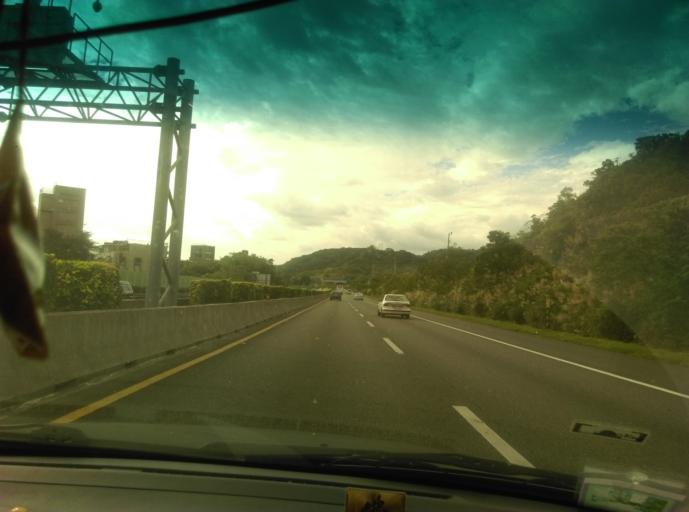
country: TW
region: Taiwan
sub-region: Keelung
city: Keelung
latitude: 25.1024
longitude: 121.7158
